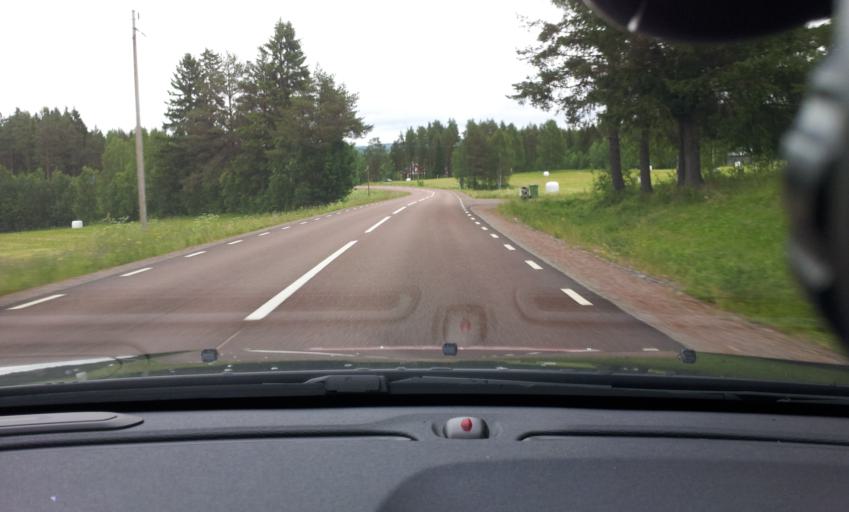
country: SE
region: Jaemtland
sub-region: Ragunda Kommun
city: Hammarstrand
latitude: 63.0189
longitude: 16.5791
